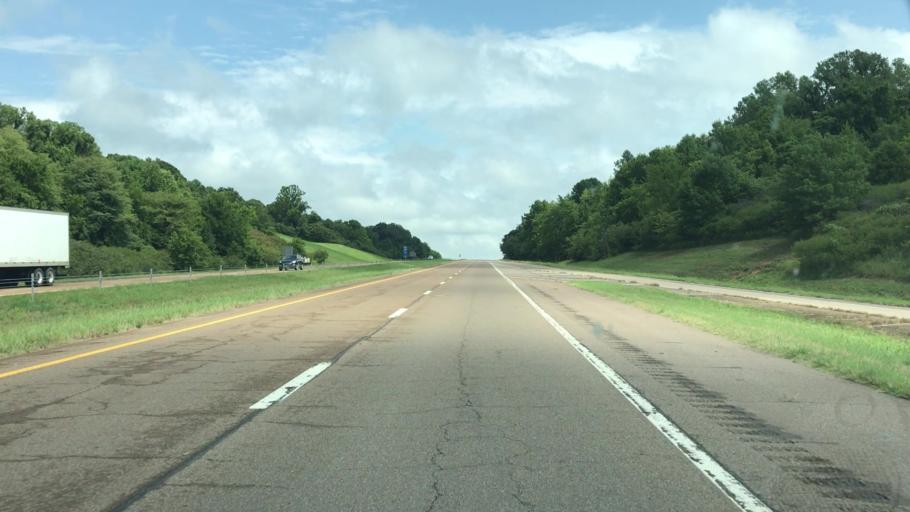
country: US
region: Tennessee
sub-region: Dyer County
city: Dyersburg
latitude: 36.0750
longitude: -89.4933
